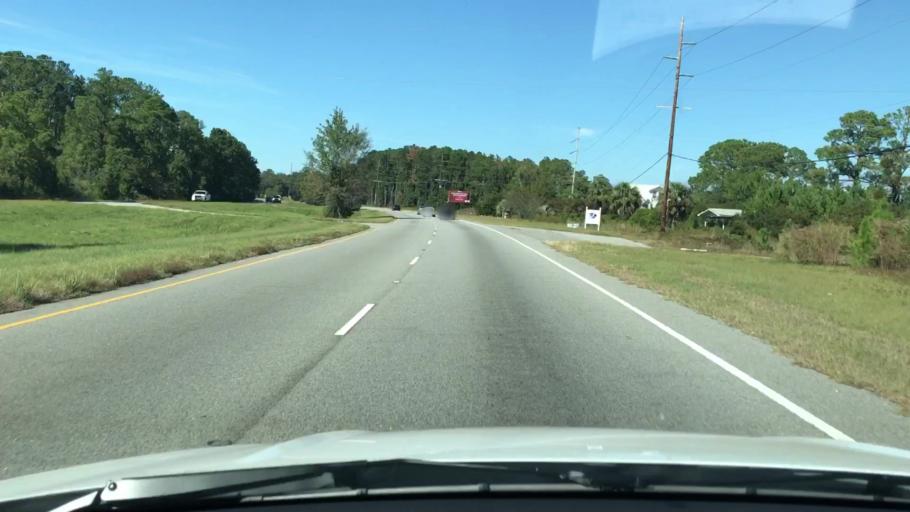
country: US
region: South Carolina
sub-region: Beaufort County
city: Laurel Bay
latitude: 32.5062
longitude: -80.7453
